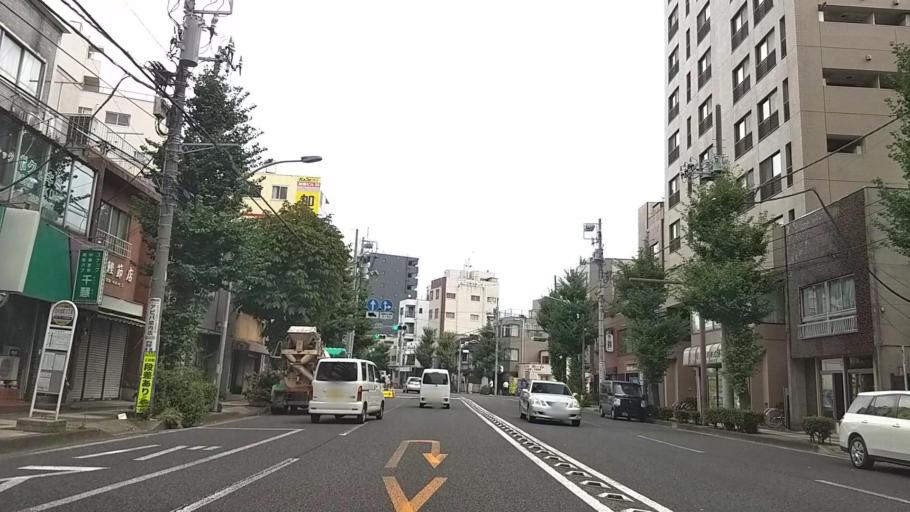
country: JP
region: Kanagawa
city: Yokohama
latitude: 35.4420
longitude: 139.6250
